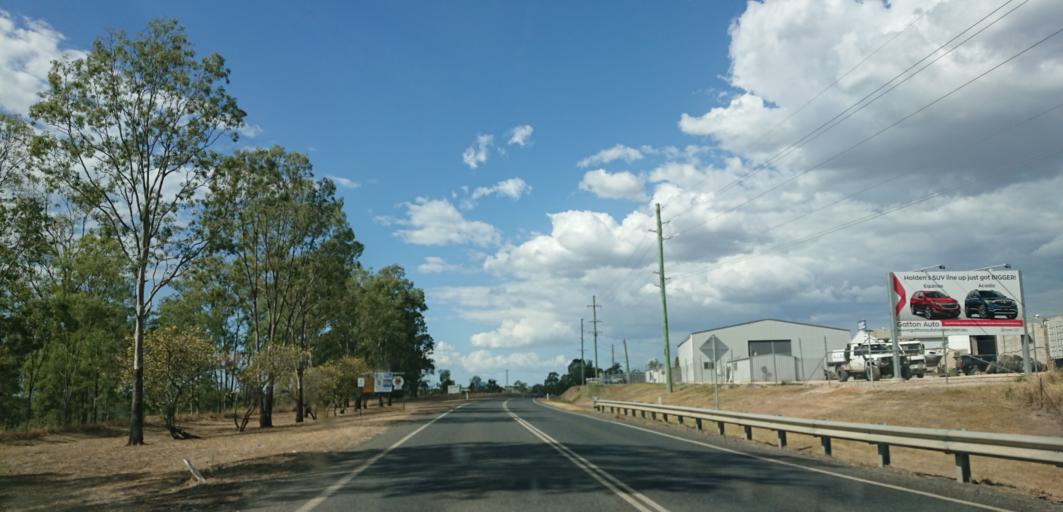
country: AU
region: Queensland
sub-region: Lockyer Valley
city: Gatton
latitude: -27.5721
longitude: 152.2576
